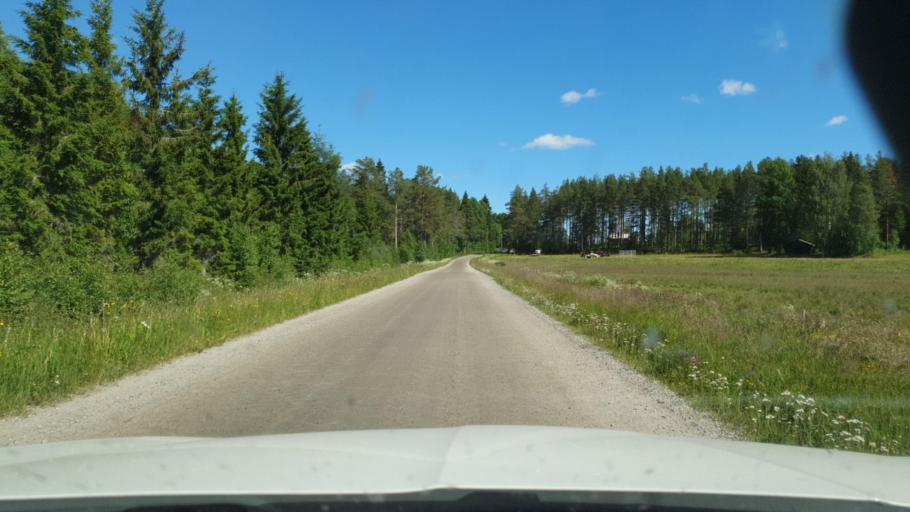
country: SE
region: Vaesterbotten
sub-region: Skelleftea Kommun
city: Byske
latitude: 65.1125
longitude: 21.1982
